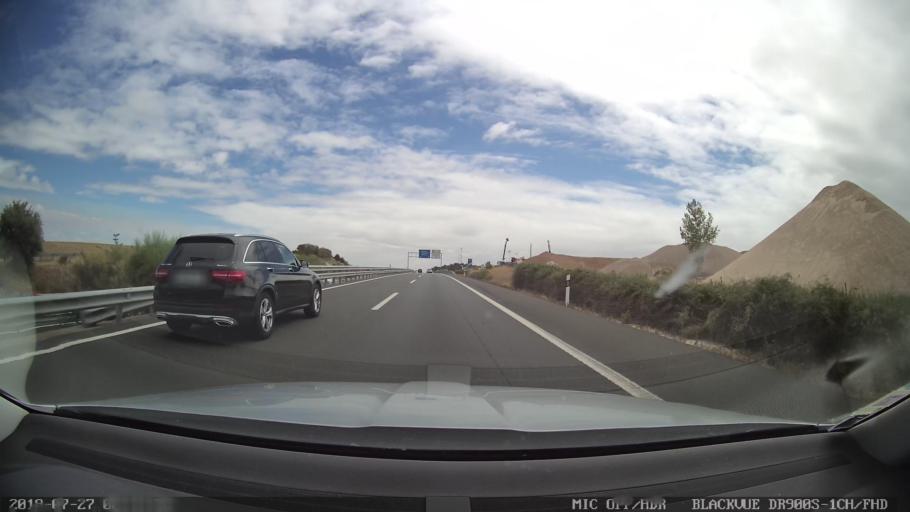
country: ES
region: Extremadura
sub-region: Provincia de Caceres
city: Peraleda de la Mata
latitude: 39.8889
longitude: -5.4727
